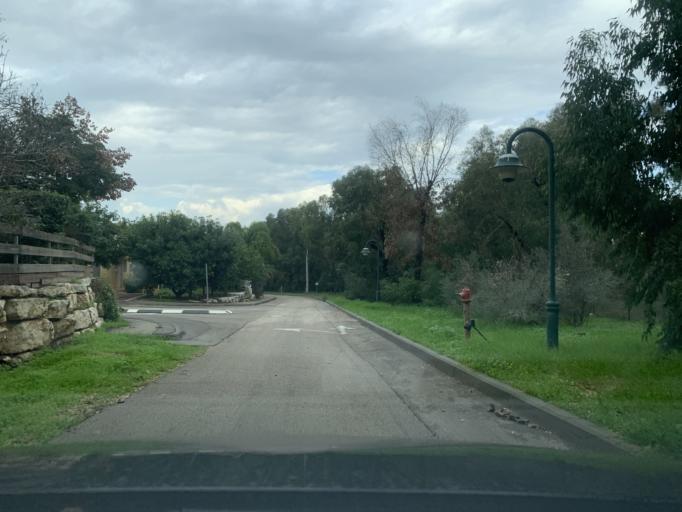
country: PS
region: West Bank
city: Qalqilyah
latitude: 32.2136
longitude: 34.9821
